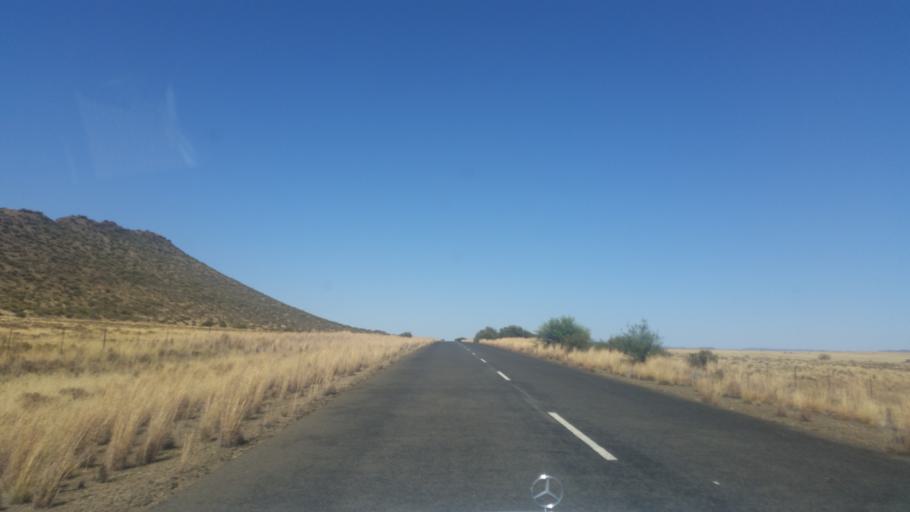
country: ZA
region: Orange Free State
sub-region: Xhariep District Municipality
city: Trompsburg
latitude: -30.5496
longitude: 25.6881
